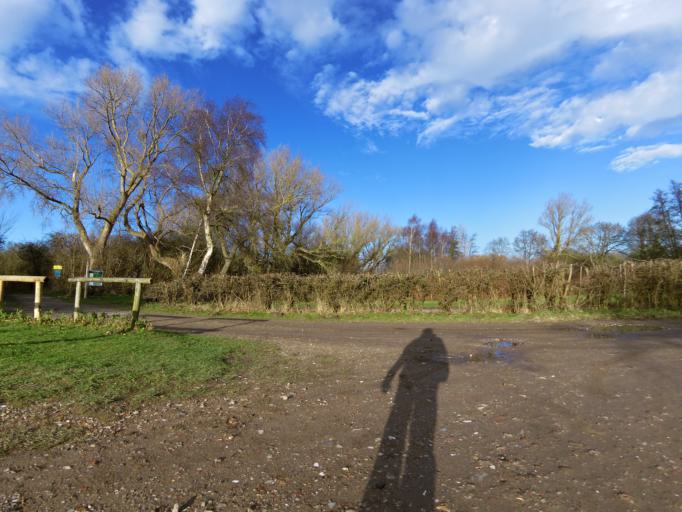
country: NL
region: South Holland
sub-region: Gemeente Hellevoetsluis
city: Nieuw-Helvoet
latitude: 51.8794
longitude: 4.0528
